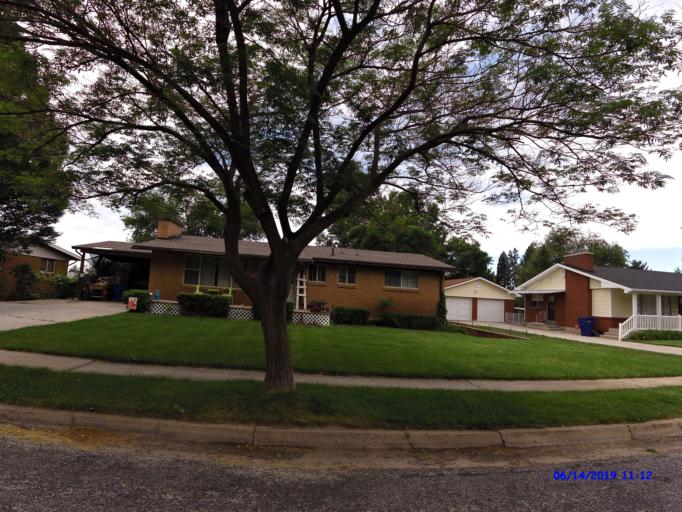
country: US
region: Utah
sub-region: Weber County
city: Ogden
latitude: 41.2463
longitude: -111.9401
